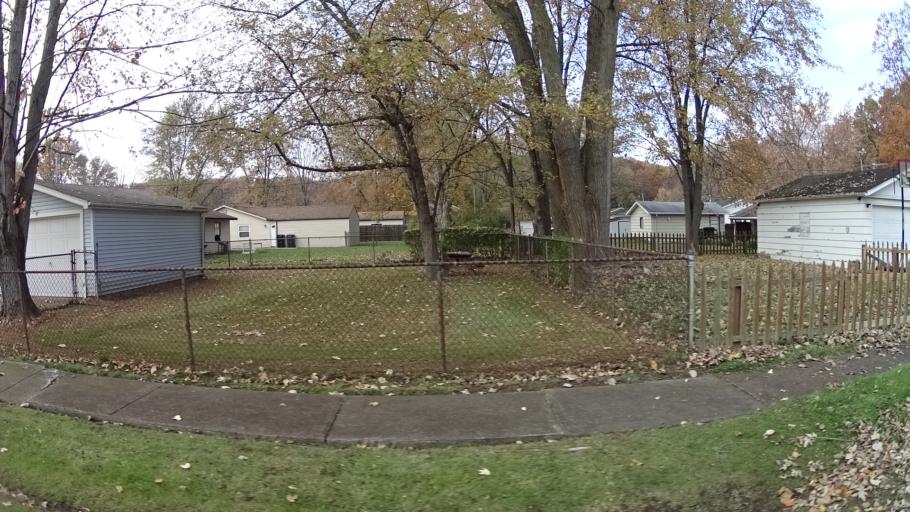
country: US
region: Ohio
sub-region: Lorain County
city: Elyria
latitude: 41.3601
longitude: -82.0861
